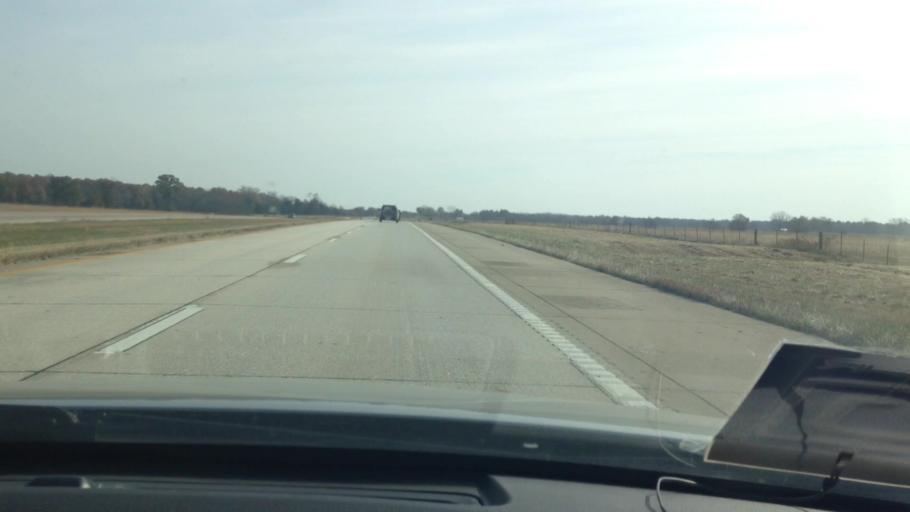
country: US
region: Missouri
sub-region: Henry County
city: Clinton
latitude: 38.4101
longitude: -93.8520
